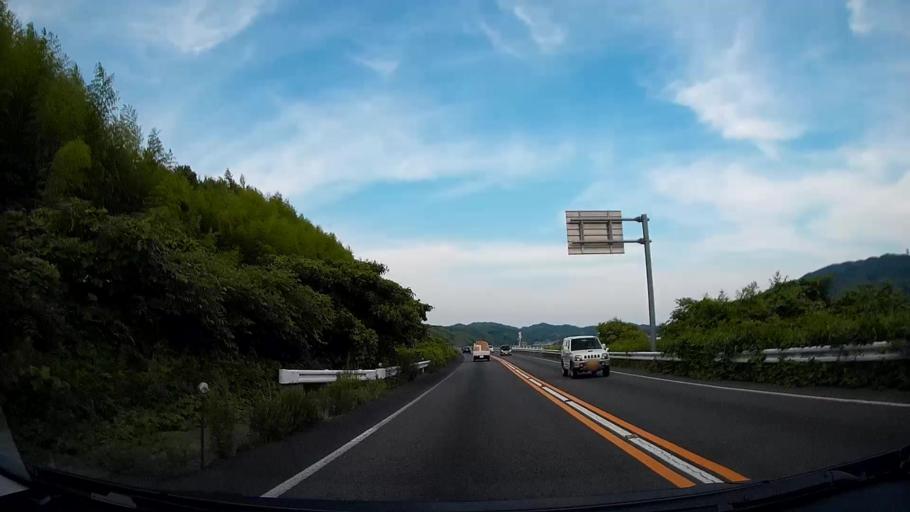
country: JP
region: Aichi
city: Nishio
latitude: 34.8616
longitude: 137.1065
